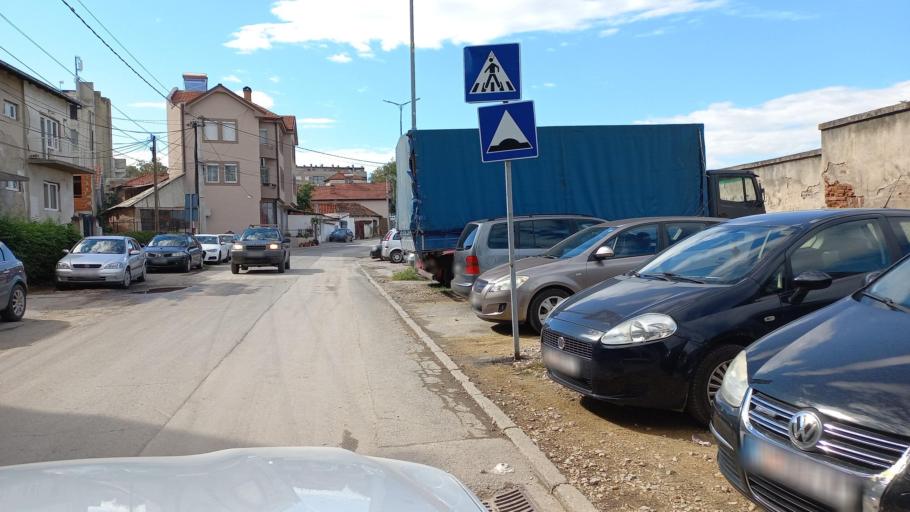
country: MK
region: Kumanovo
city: Kumanovo
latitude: 42.1392
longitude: 21.7151
